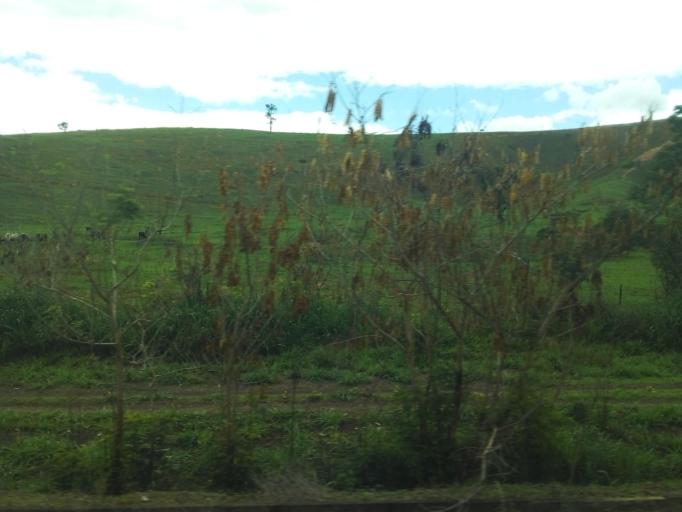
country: BR
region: Minas Gerais
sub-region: Governador Valadares
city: Governador Valadares
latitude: -19.0743
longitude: -42.1548
